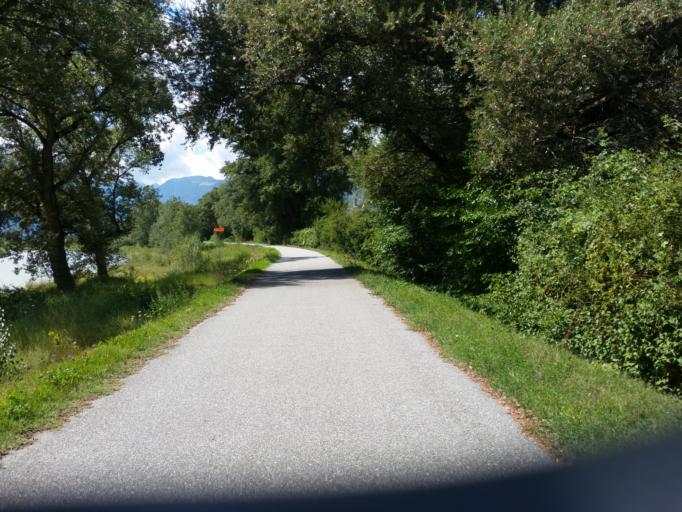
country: CH
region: Valais
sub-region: Martigny District
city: Leytron
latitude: 46.1776
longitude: 7.2058
